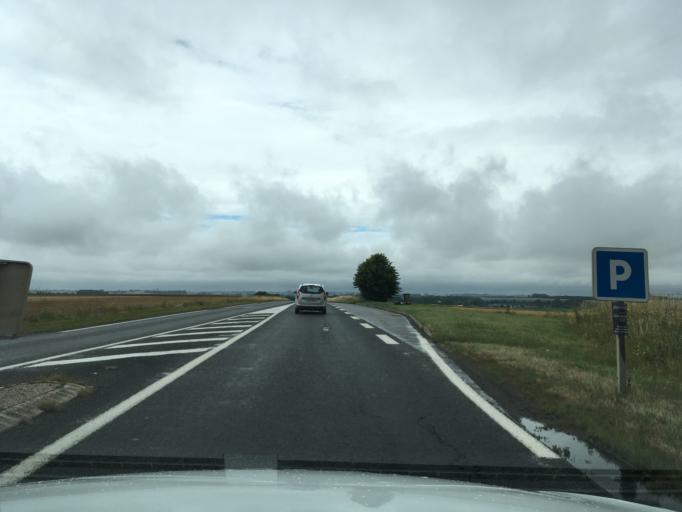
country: FR
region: Picardie
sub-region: Departement de l'Aisne
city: Homblieres
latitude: 49.8454
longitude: 3.3918
